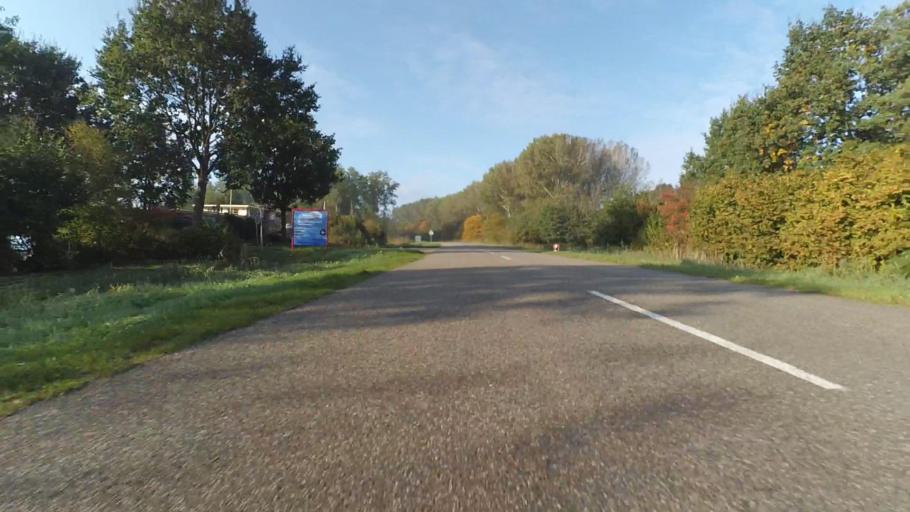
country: NL
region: Gelderland
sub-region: Gemeente Nijkerk
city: Nijkerk
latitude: 52.2705
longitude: 5.4889
